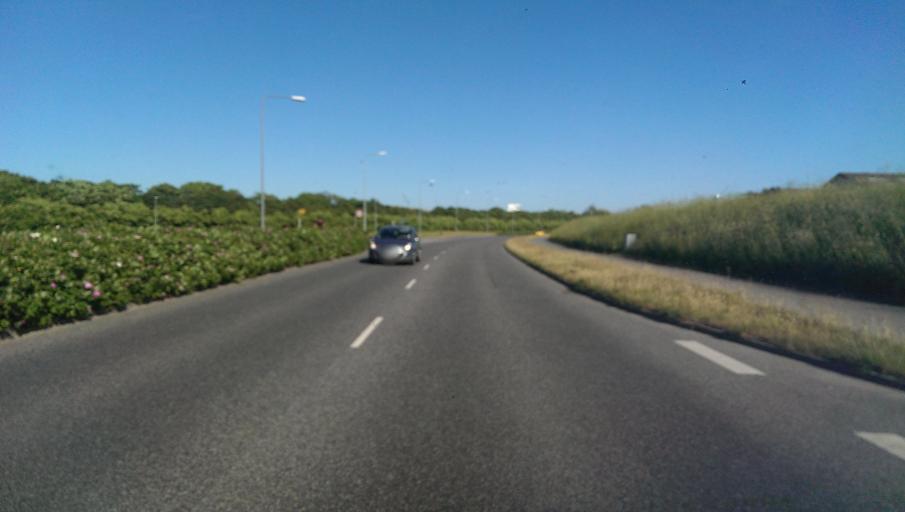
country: DK
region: South Denmark
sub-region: Esbjerg Kommune
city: Esbjerg
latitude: 55.4842
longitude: 8.4222
